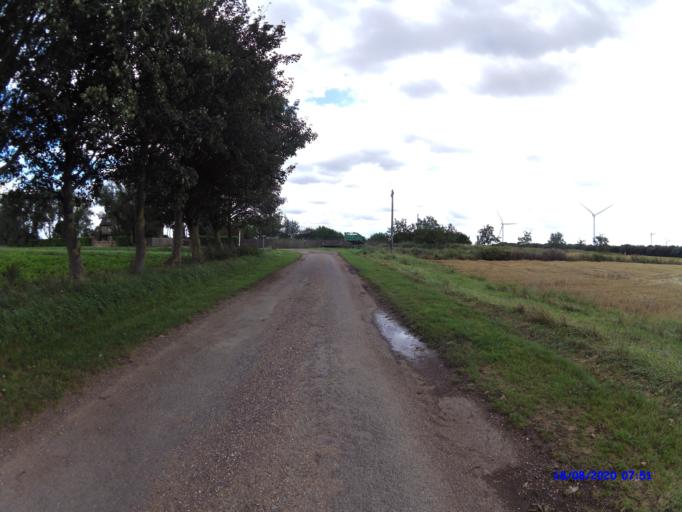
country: GB
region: England
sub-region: Cambridgeshire
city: Whittlesey
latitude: 52.5188
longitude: -0.0925
